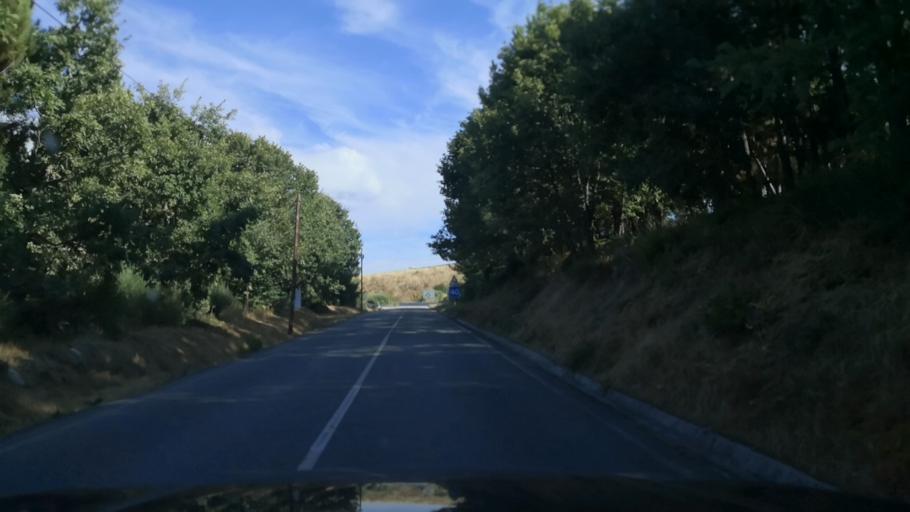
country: PT
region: Vila Real
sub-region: Murca
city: Murca
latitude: 41.3755
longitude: -7.5450
